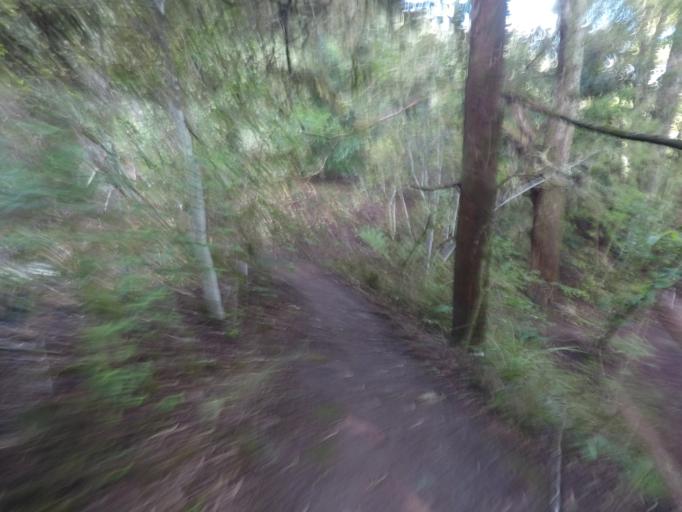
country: NZ
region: Auckland
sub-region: Auckland
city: Rothesay Bay
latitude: -36.7371
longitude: 174.7030
